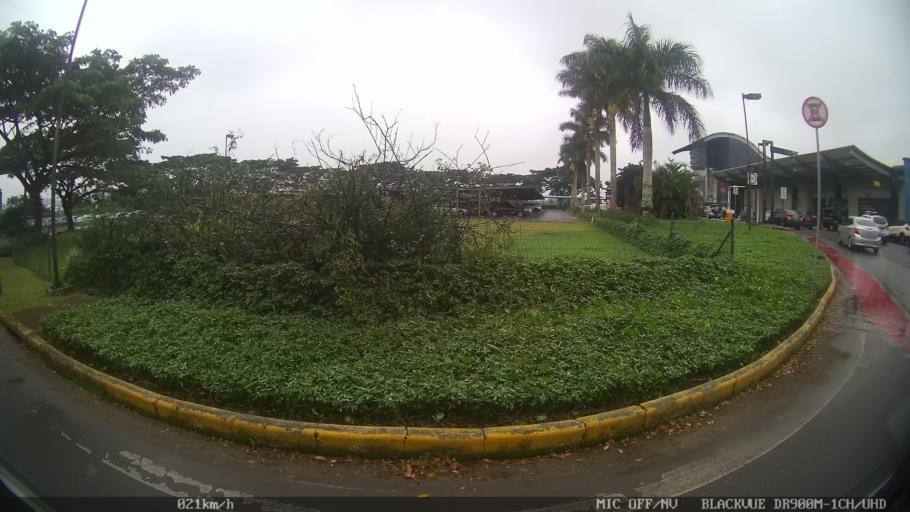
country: BR
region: Santa Catarina
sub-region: Joinville
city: Joinville
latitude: -26.2249
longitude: -48.8014
